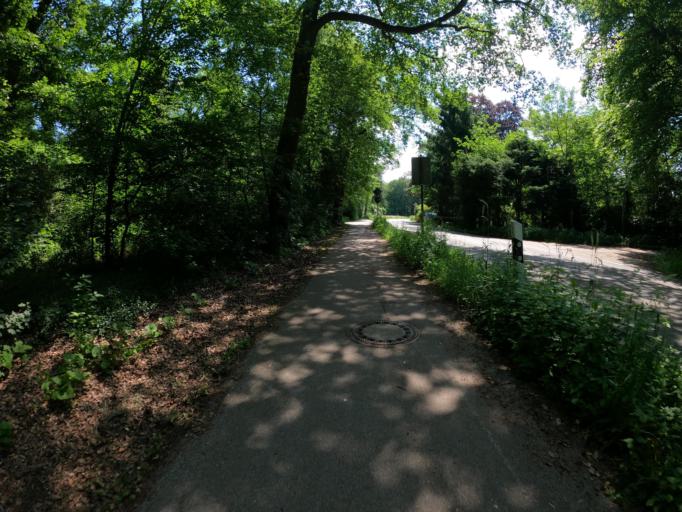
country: DE
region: North Rhine-Westphalia
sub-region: Regierungsbezirk Dusseldorf
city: Hunxe
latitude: 51.7105
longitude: 6.7786
